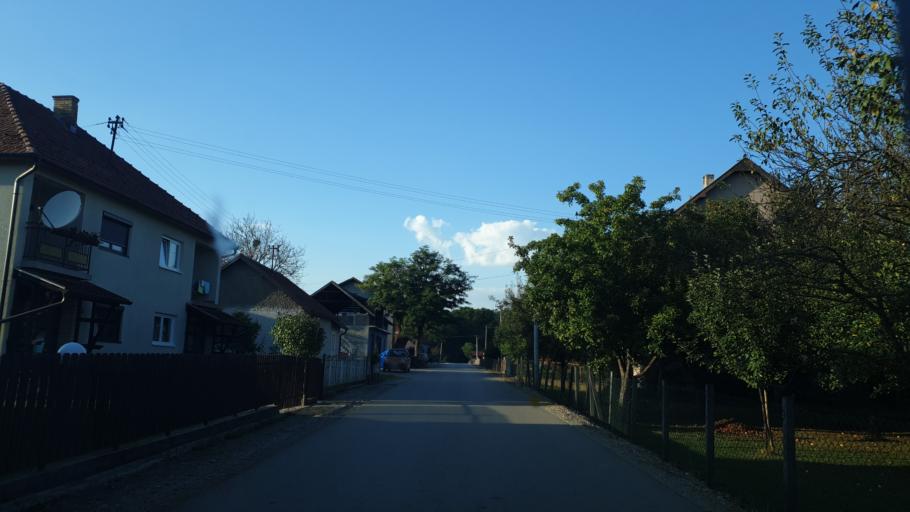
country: RS
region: Central Serbia
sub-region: Zlatiborski Okrug
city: Pozega
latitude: 43.8698
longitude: 19.9913
